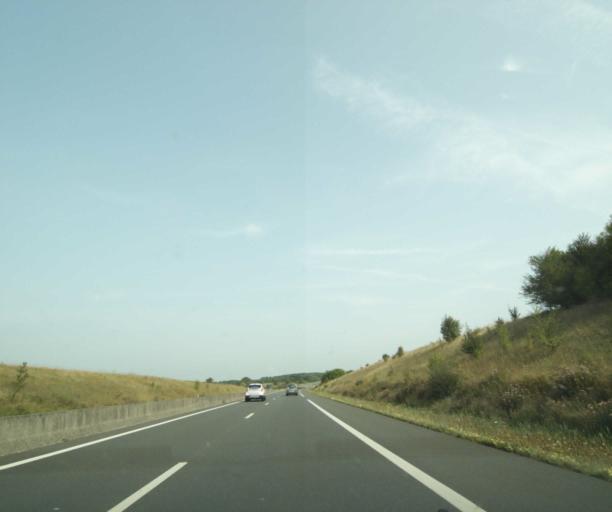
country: FR
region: Pays de la Loire
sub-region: Departement de la Sarthe
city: Beaumont-sur-Sarthe
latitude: 48.2776
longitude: 0.1579
